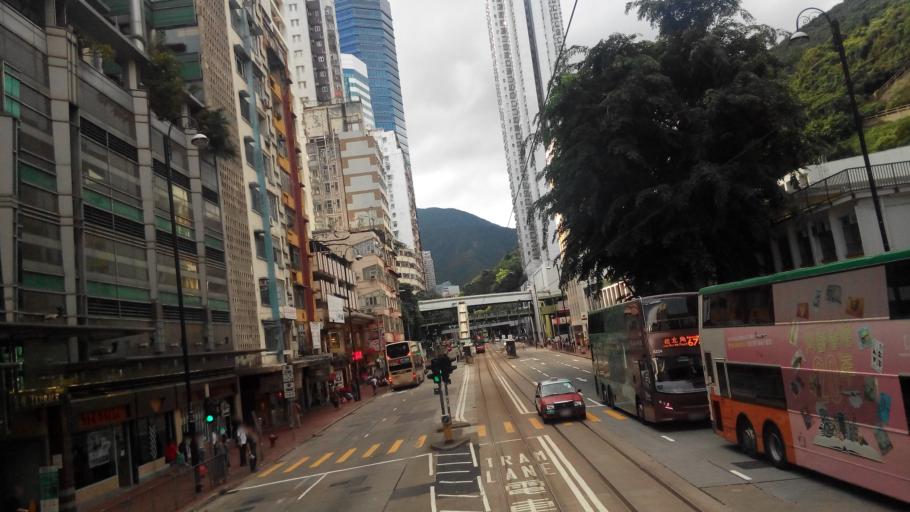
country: HK
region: Kowloon City
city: Kowloon
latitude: 22.2899
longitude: 114.2094
